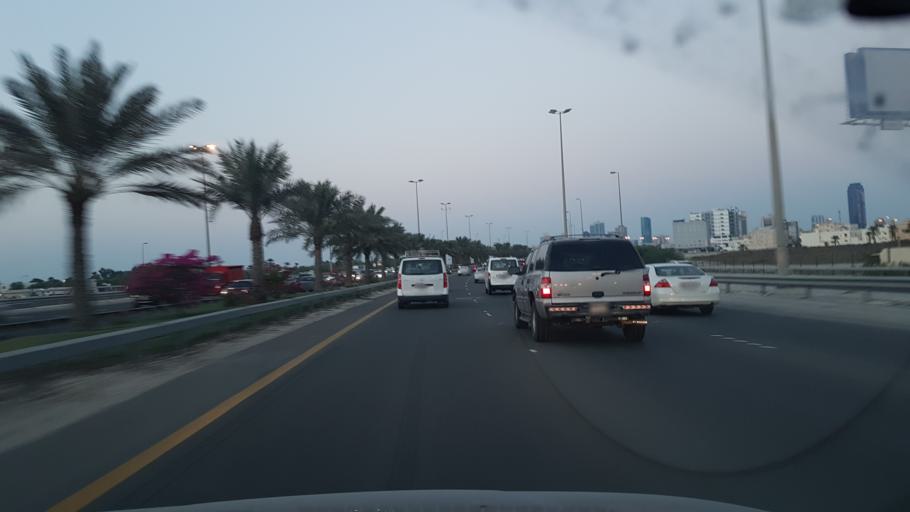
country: BH
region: Manama
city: Jidd Hafs
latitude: 26.2215
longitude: 50.5223
